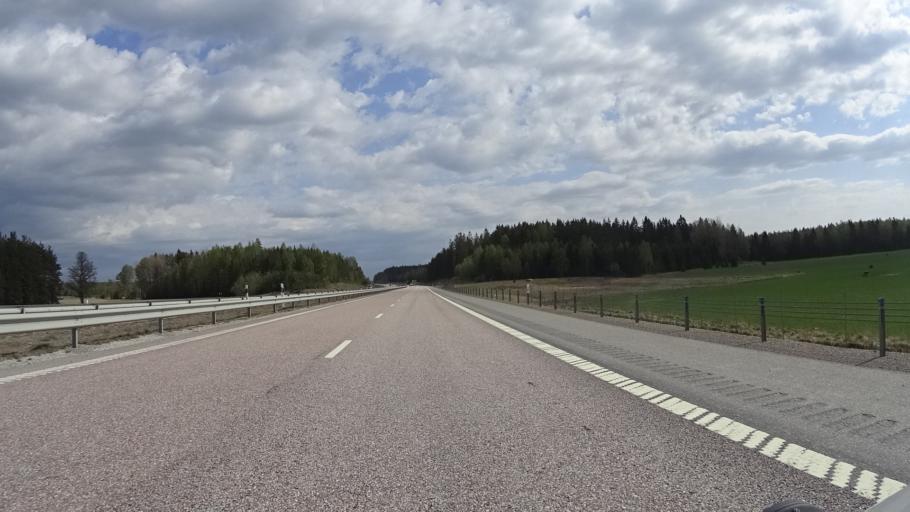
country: SE
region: Soedermanland
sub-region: Strangnas Kommun
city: Akers Styckebruk
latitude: 59.3117
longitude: 17.0621
